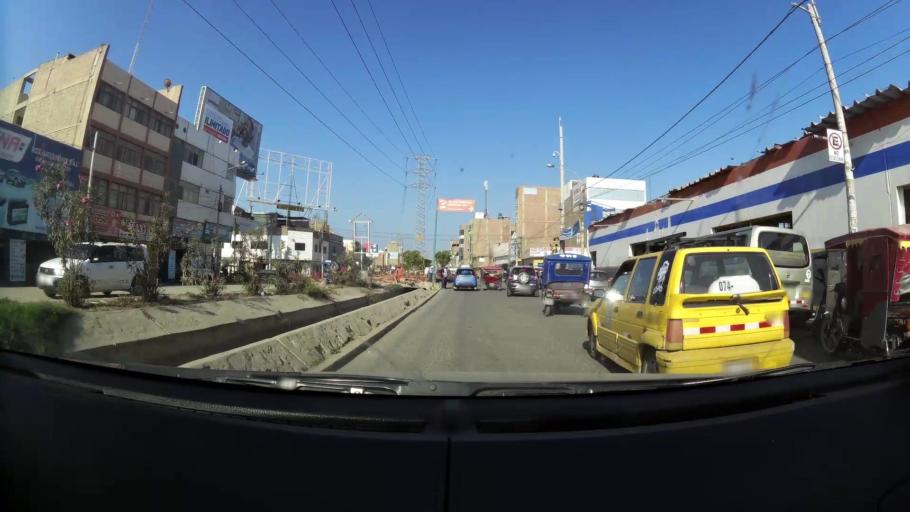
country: PE
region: Lambayeque
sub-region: Provincia de Chiclayo
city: Chiclayo
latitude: -6.7626
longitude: -79.8418
